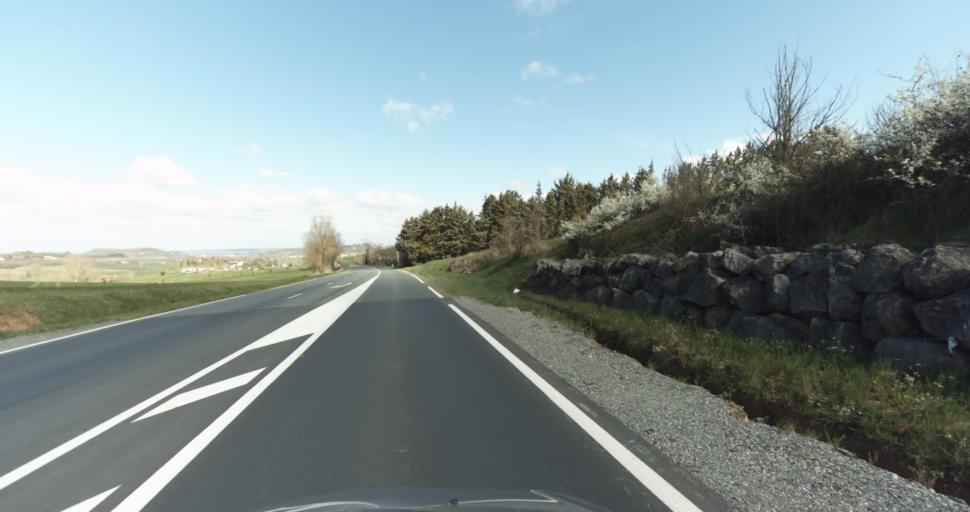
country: FR
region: Midi-Pyrenees
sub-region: Departement du Tarn
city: Puygouzon
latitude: 43.8666
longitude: 2.1863
